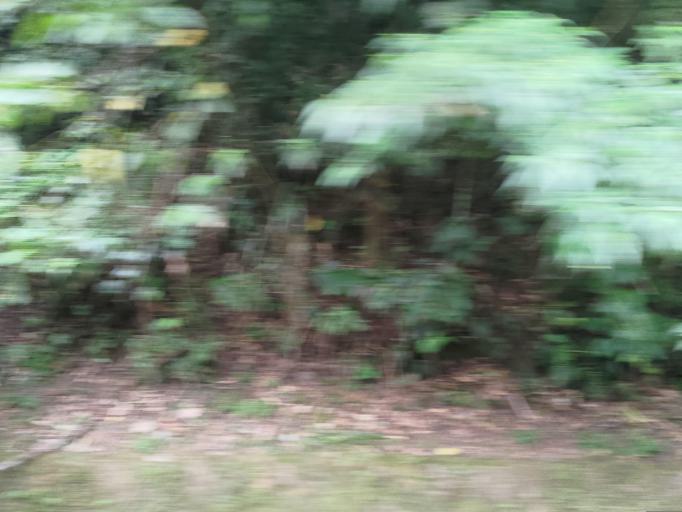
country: TW
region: Taiwan
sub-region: Hsinchu
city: Hsinchu
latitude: 24.6014
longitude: 121.0372
